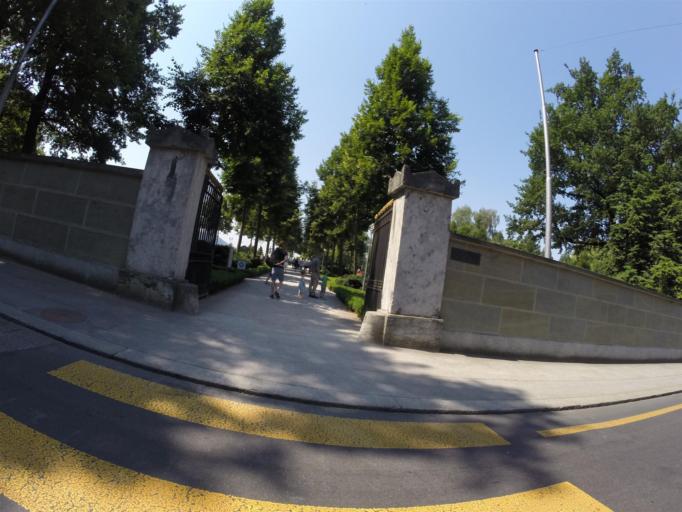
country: CH
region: Bern
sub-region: Bern-Mittelland District
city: Bern
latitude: 46.9524
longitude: 7.4611
